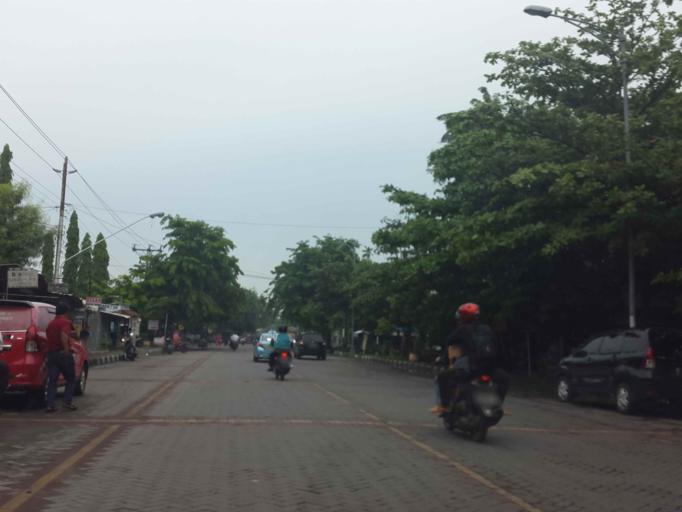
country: ID
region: Central Java
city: Semarang
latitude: -6.9677
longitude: 110.4251
